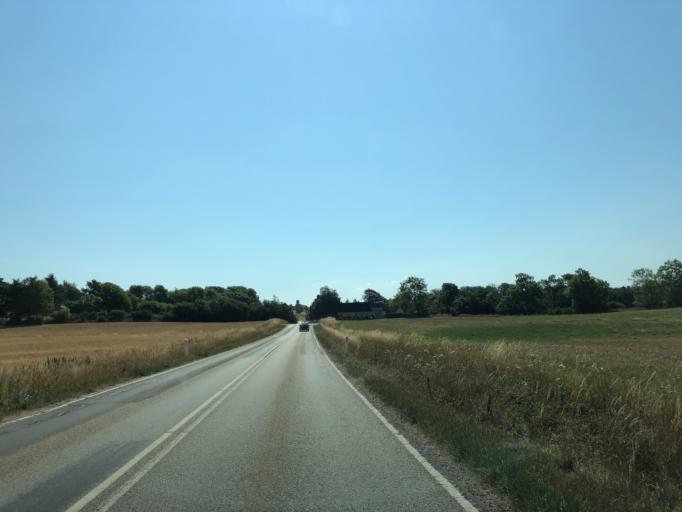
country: DK
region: Zealand
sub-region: Odsherred Kommune
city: Nykobing Sjaelland
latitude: 55.9259
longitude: 11.6362
